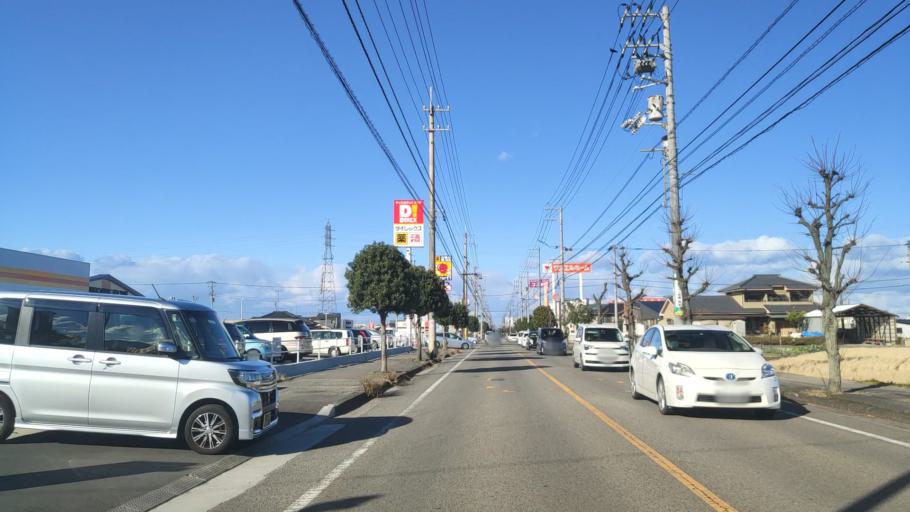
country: JP
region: Ehime
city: Saijo
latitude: 33.9241
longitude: 133.1912
